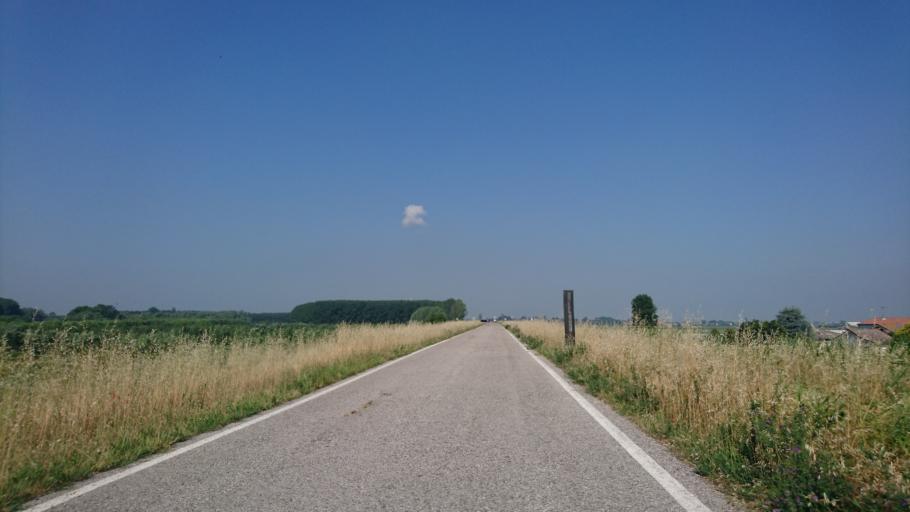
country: IT
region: Veneto
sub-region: Provincia di Rovigo
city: Melara
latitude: 45.0613
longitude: 11.1959
